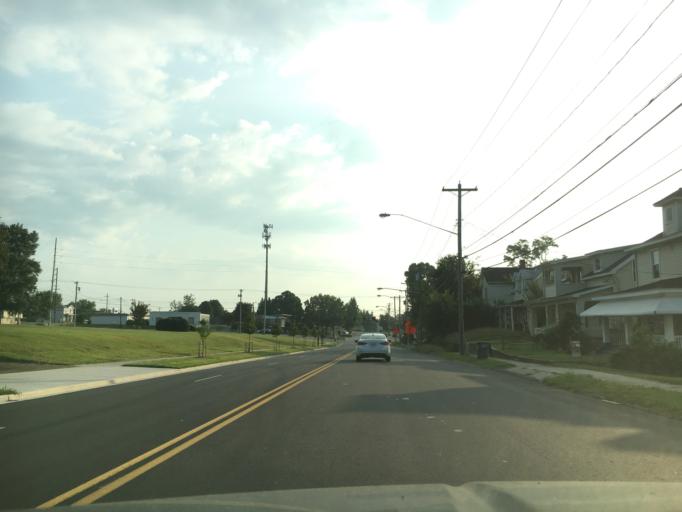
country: US
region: Virginia
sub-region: City of Lynchburg
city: West Lynchburg
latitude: 37.4066
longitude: -79.1655
